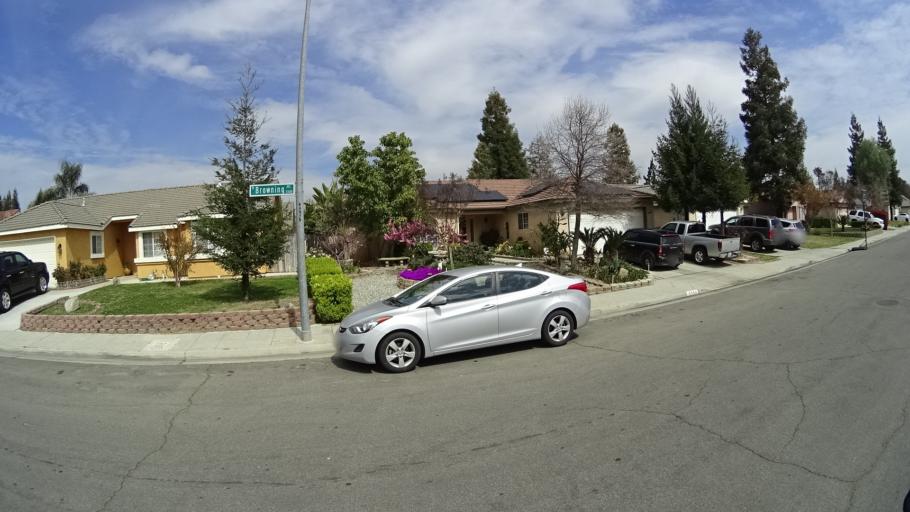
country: US
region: California
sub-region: Fresno County
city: West Park
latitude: 36.8186
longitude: -119.8872
